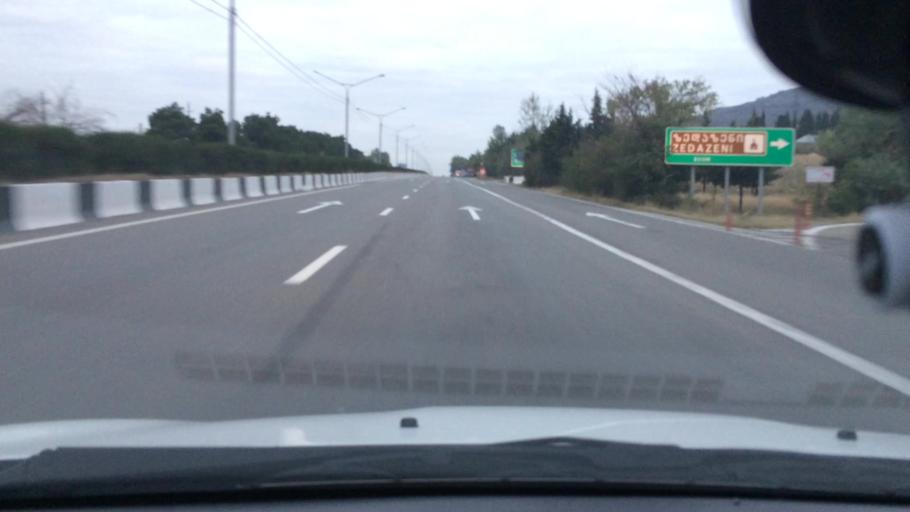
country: GE
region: Mtskheta-Mtianeti
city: Mtskheta
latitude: 41.8563
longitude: 44.7316
